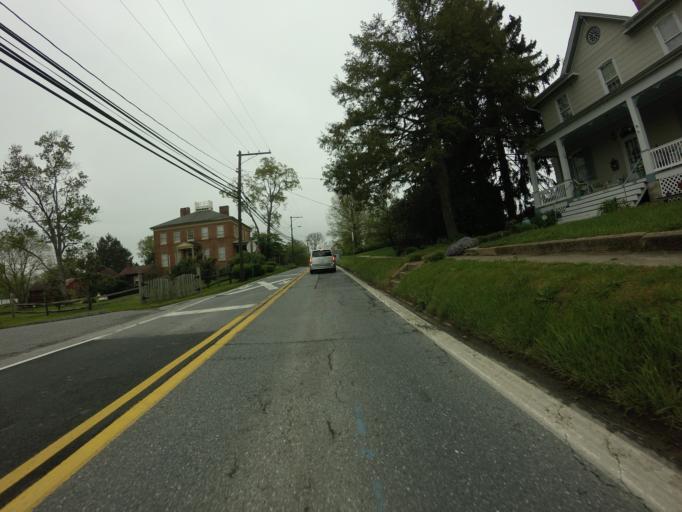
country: US
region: Maryland
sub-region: Carroll County
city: New Windsor
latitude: 39.5270
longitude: -77.1024
